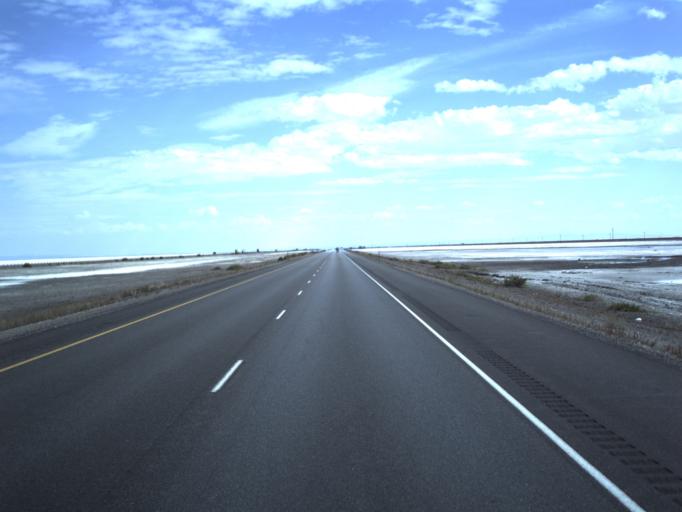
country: US
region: Utah
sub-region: Tooele County
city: Wendover
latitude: 40.7396
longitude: -113.9094
